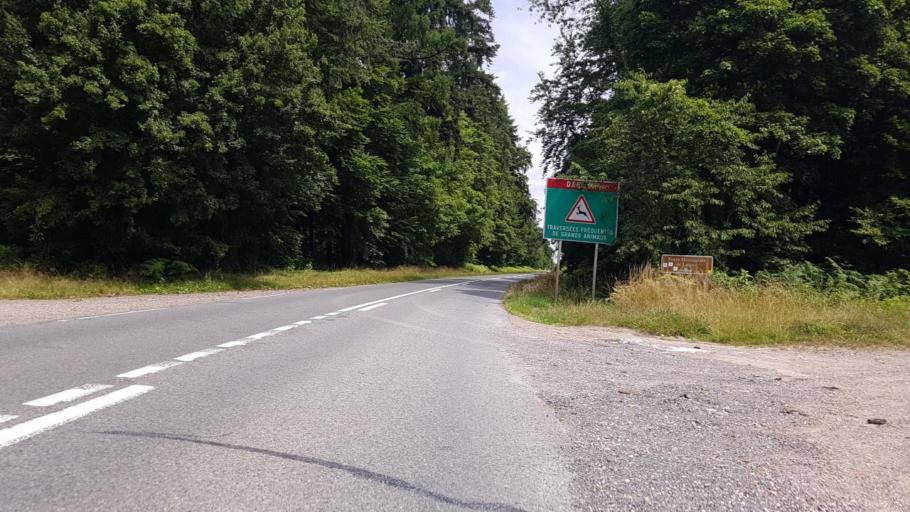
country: FR
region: Picardie
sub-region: Departement de l'Oise
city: Le Plessis-Brion
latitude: 49.4459
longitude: 2.8956
